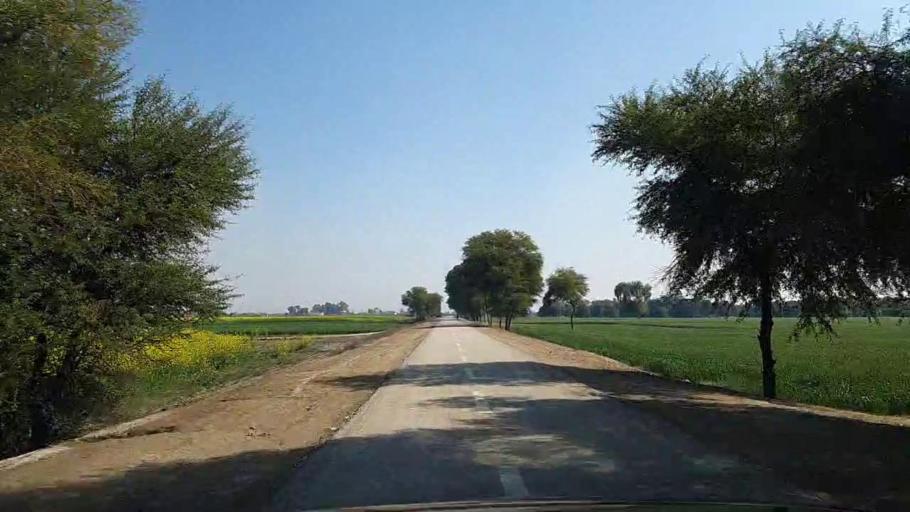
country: PK
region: Sindh
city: Nawabshah
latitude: 26.3201
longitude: 68.3383
